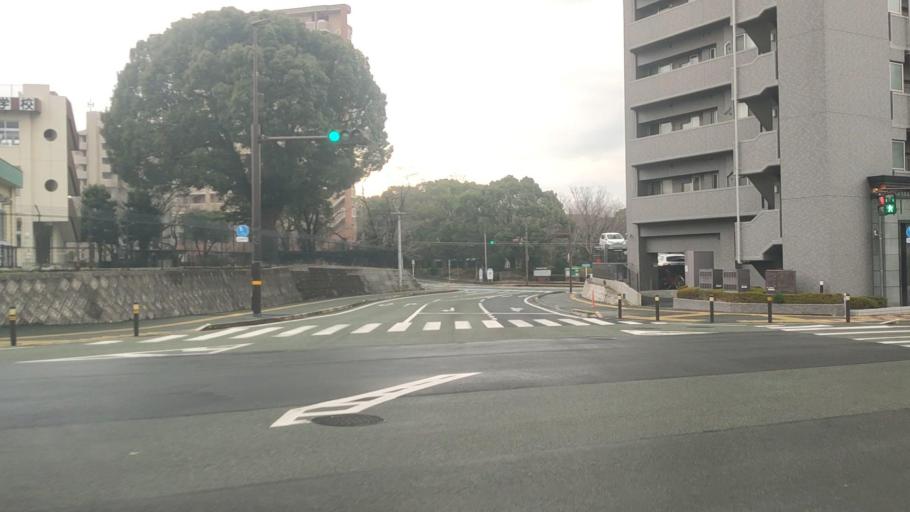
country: JP
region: Kumamoto
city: Kumamoto
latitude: 32.7876
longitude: 130.7377
